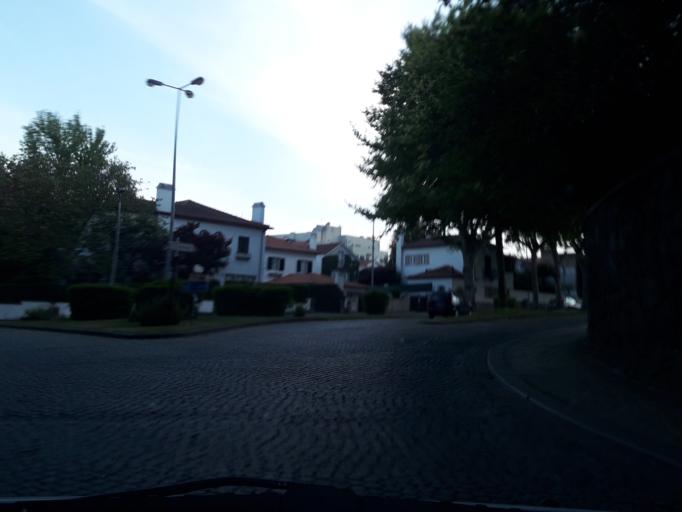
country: PT
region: Braga
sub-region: Vila Nova de Famalicao
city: Calendario
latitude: 41.4072
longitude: -8.5254
